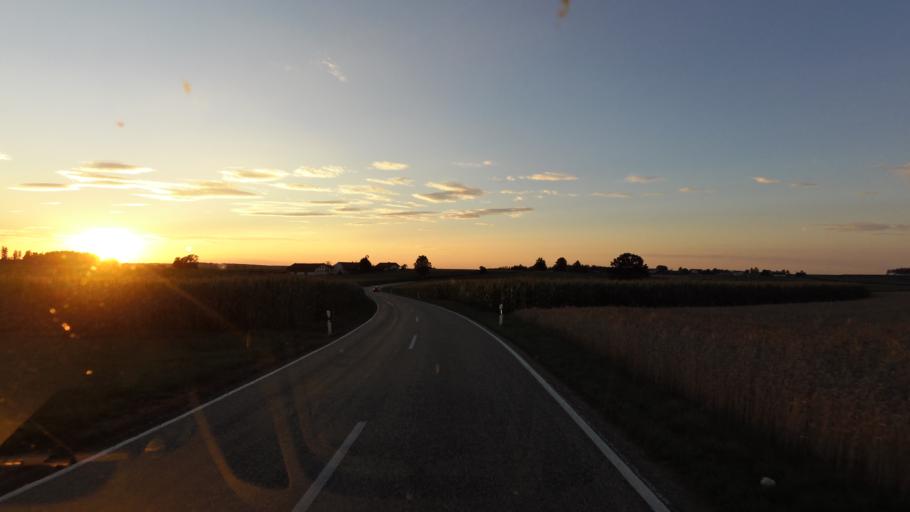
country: DE
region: Bavaria
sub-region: Upper Bavaria
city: Taufkirchen
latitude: 48.1039
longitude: 12.4753
